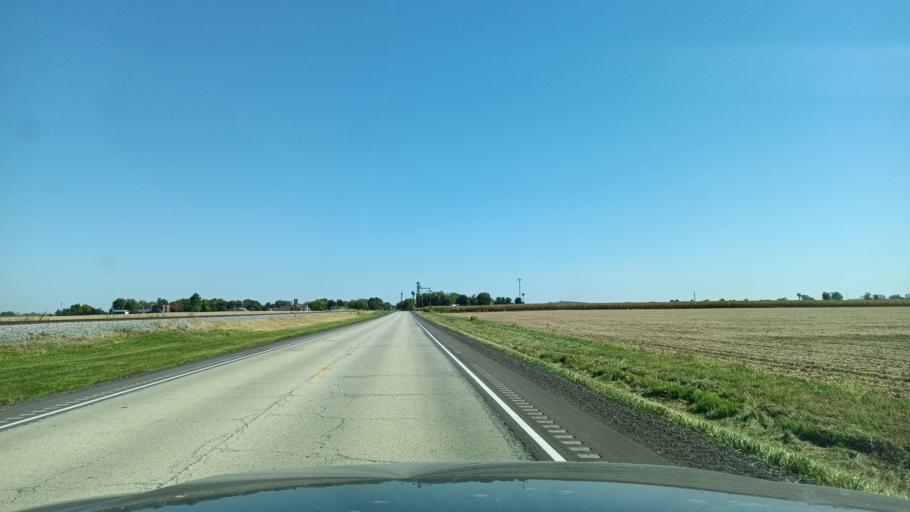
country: US
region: Illinois
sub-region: Woodford County
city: Eureka
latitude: 40.6272
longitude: -89.2924
